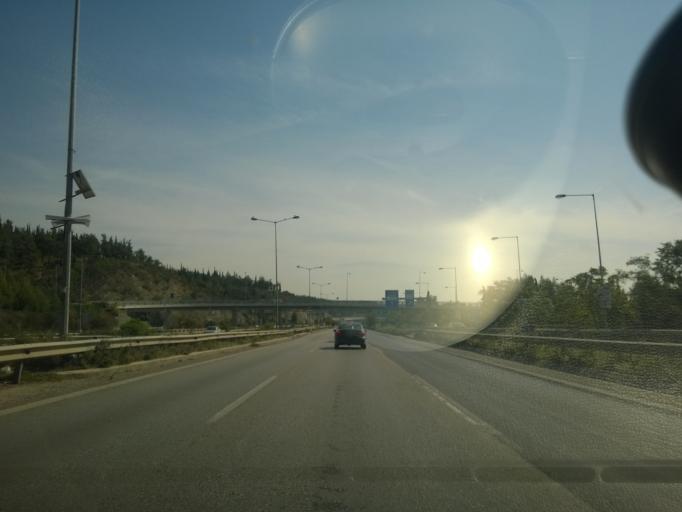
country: GR
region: Central Macedonia
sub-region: Nomos Thessalonikis
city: Triandria
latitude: 40.6268
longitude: 22.9784
